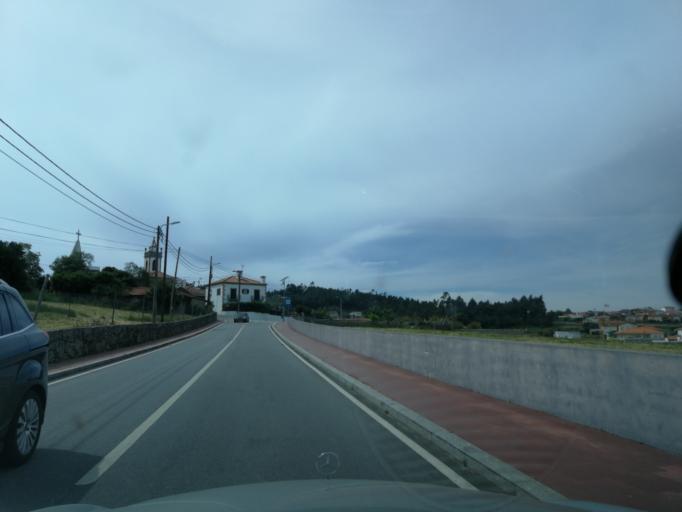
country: PT
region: Braga
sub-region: Vila Nova de Famalicao
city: Calendario
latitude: 41.4114
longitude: -8.5398
